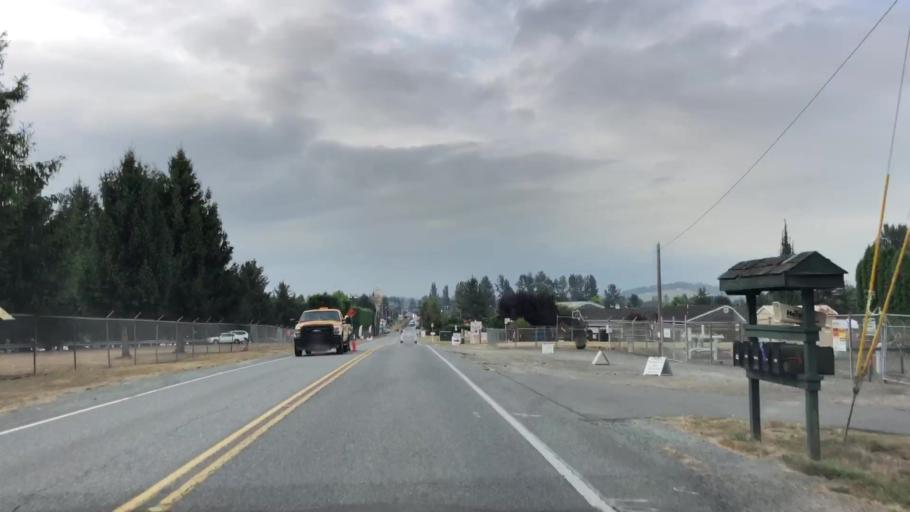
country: US
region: Washington
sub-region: Snohomish County
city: Monroe
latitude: 47.8728
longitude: -121.9906
